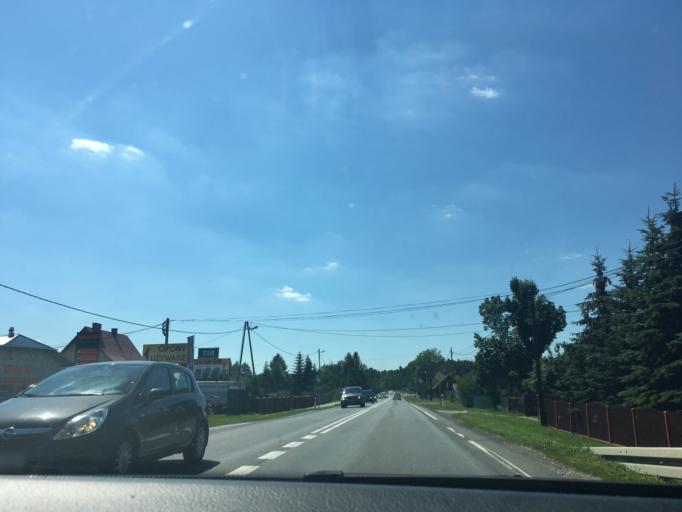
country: PL
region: Subcarpathian Voivodeship
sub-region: Powiat nizanski
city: Nisko
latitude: 50.5018
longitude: 22.1396
